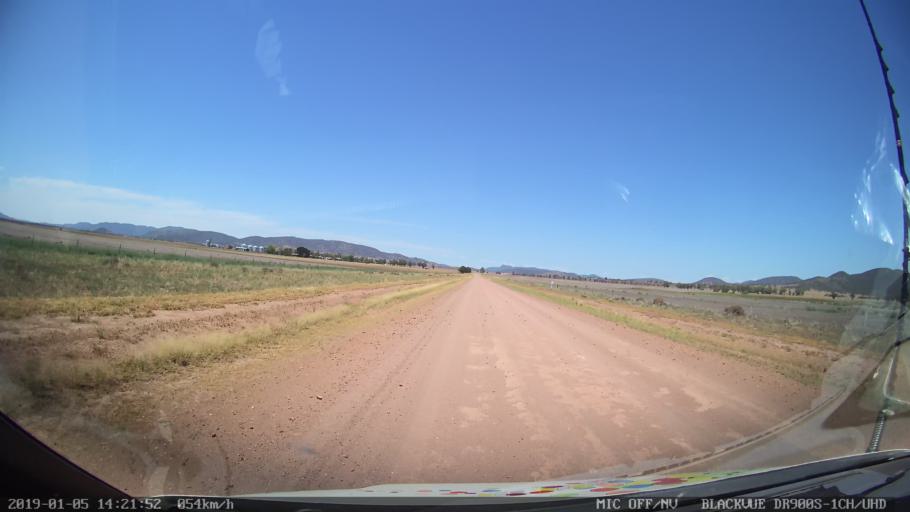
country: AU
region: New South Wales
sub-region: Liverpool Plains
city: Quirindi
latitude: -31.2457
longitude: 150.5169
